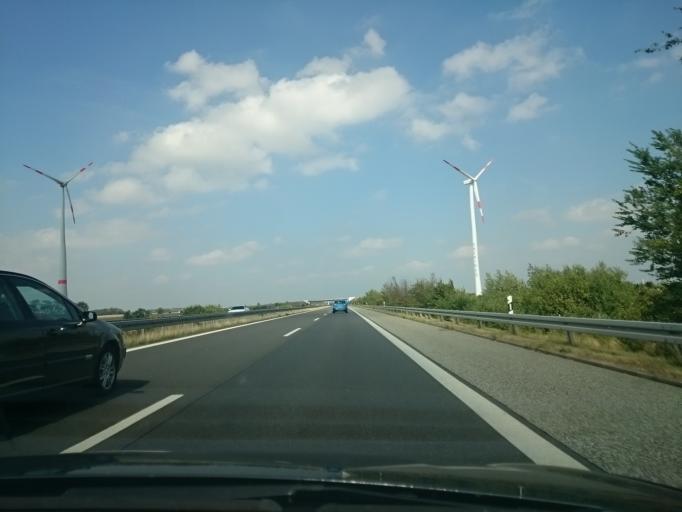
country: DE
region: Brandenburg
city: Schonfeld
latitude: 53.3865
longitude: 13.9904
